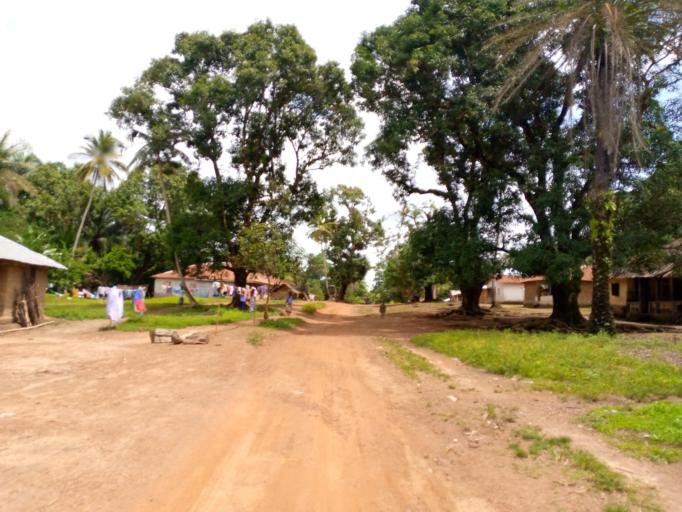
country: SL
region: Northern Province
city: Magburaka
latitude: 8.7073
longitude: -11.9647
